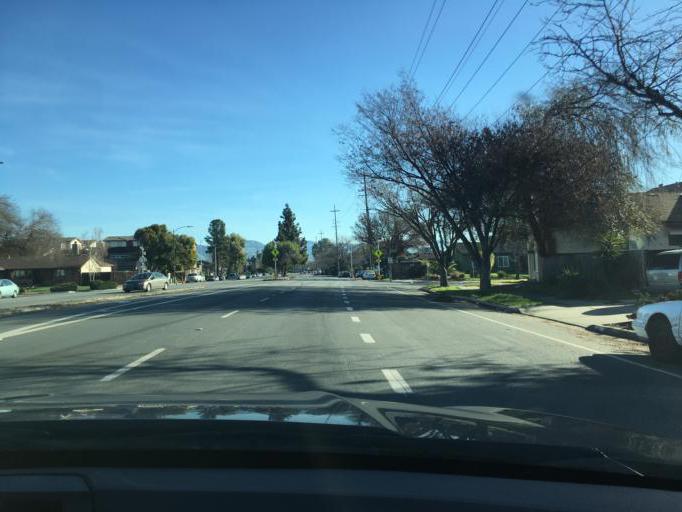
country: US
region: California
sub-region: Santa Clara County
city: Seven Trees
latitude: 37.2644
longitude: -121.8711
